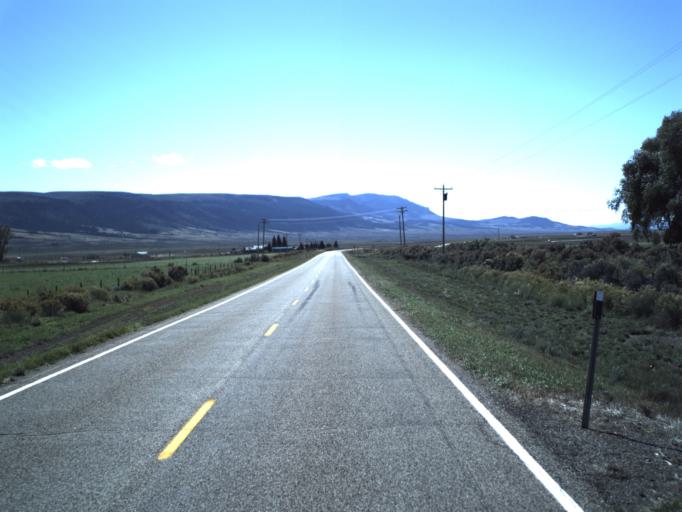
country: US
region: Utah
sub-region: Wayne County
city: Loa
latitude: 38.5004
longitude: -111.8814
